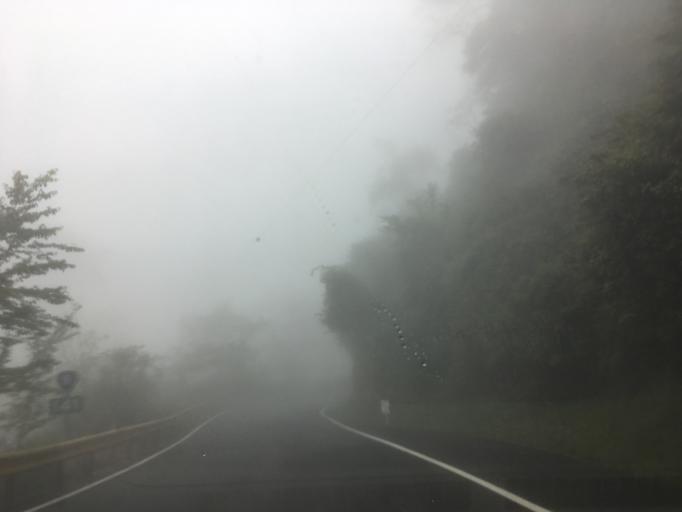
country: TW
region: Taiwan
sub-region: Hualien
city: Hualian
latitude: 24.1948
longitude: 121.4237
